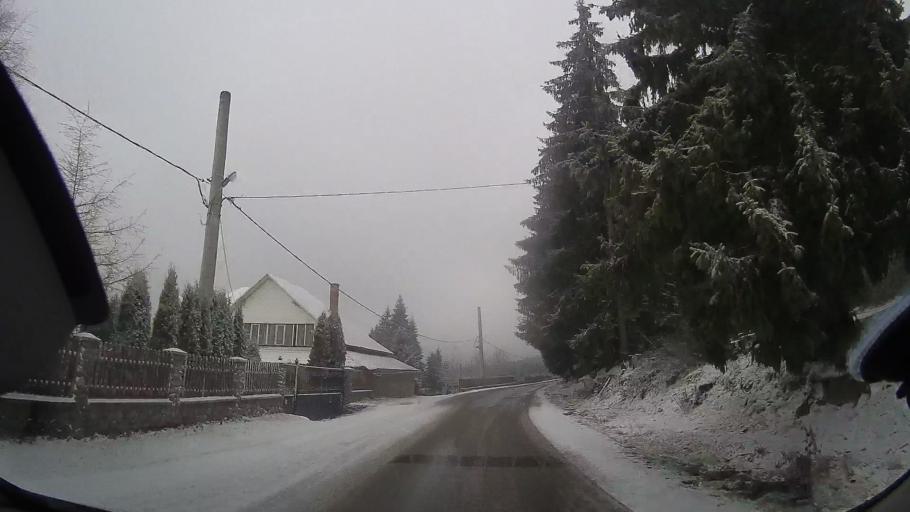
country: RO
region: Cluj
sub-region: Comuna Maguri-Racatau
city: Maguri
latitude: 46.6476
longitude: 23.0776
